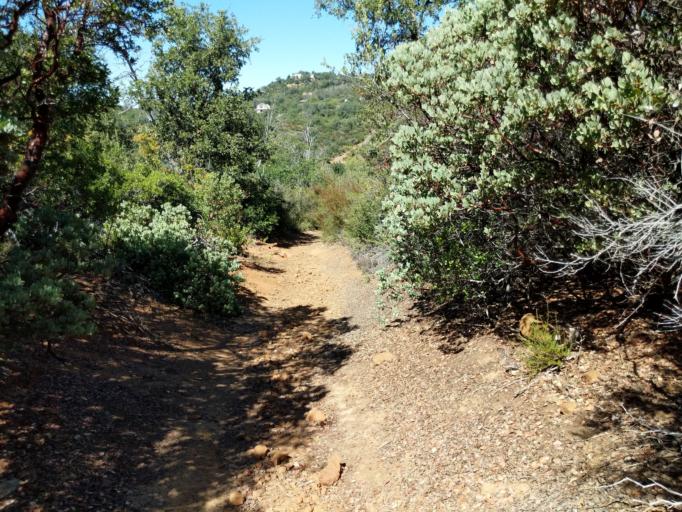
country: US
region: California
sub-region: San Diego County
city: Julian
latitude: 33.0354
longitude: -116.6303
